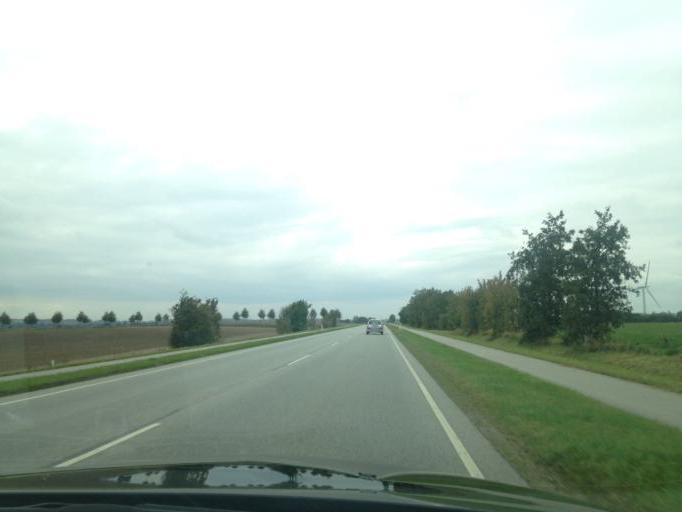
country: DK
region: South Denmark
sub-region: Kolding Kommune
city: Christiansfeld
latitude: 55.3269
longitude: 9.4930
